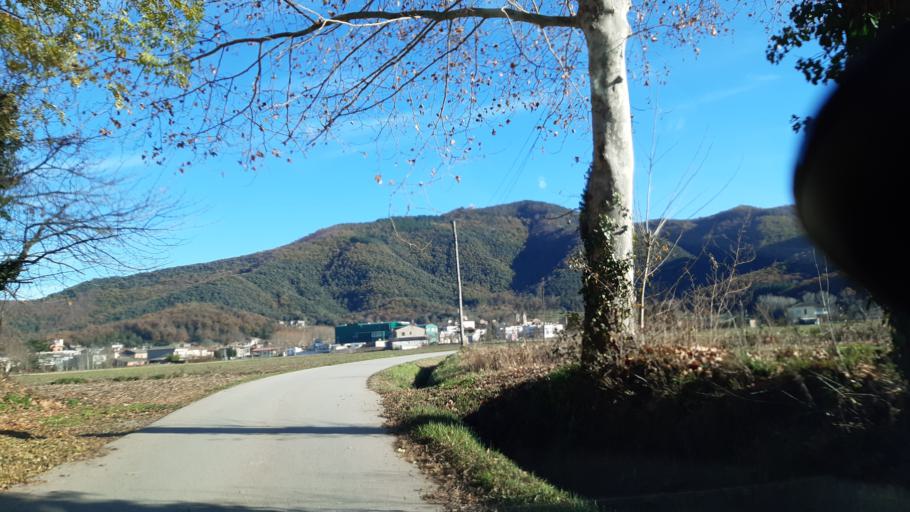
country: ES
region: Catalonia
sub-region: Provincia de Girona
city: Bas
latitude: 42.1434
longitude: 2.4508
